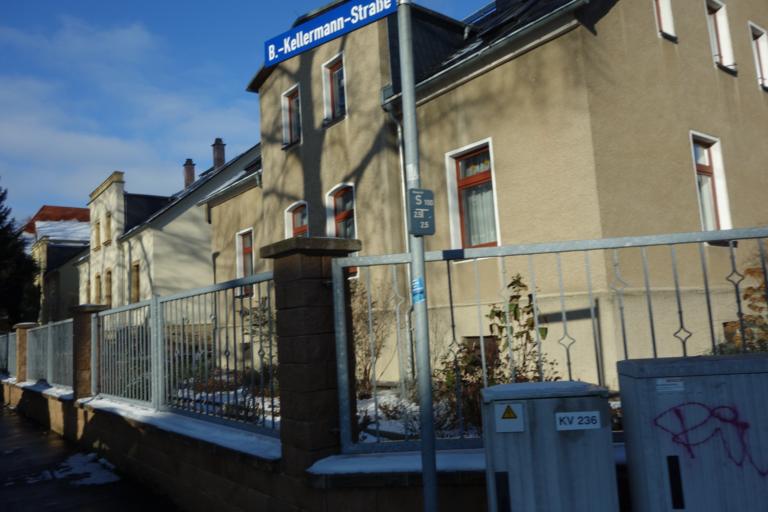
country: DE
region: Saxony
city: Freiberg
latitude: 50.9205
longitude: 13.3351
